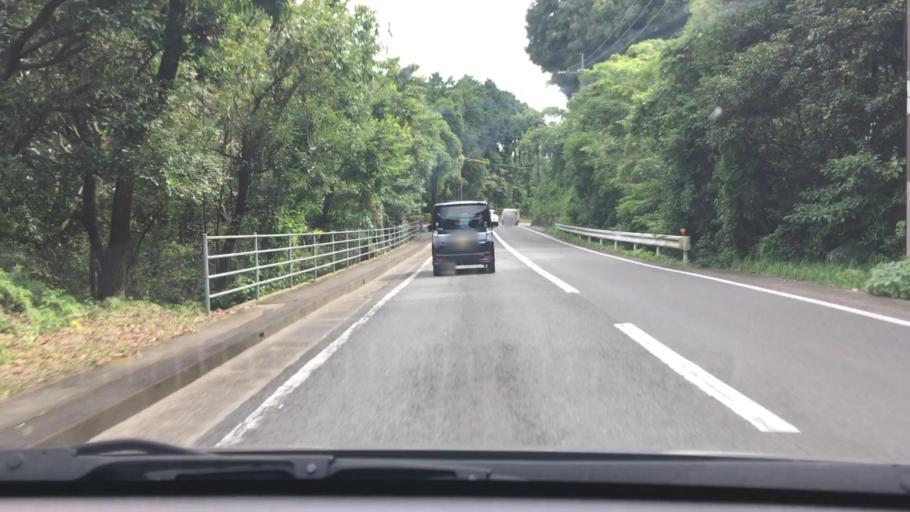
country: JP
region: Nagasaki
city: Togitsu
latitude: 32.9207
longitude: 129.7873
